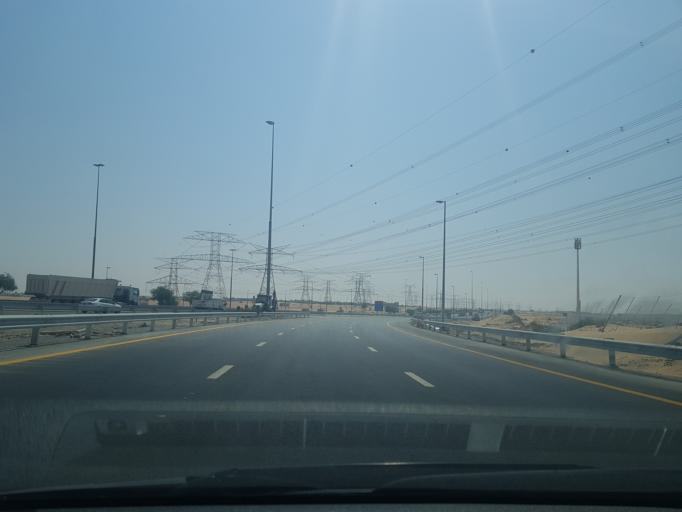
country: AE
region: Ash Shariqah
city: Sharjah
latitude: 25.2348
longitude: 55.5640
